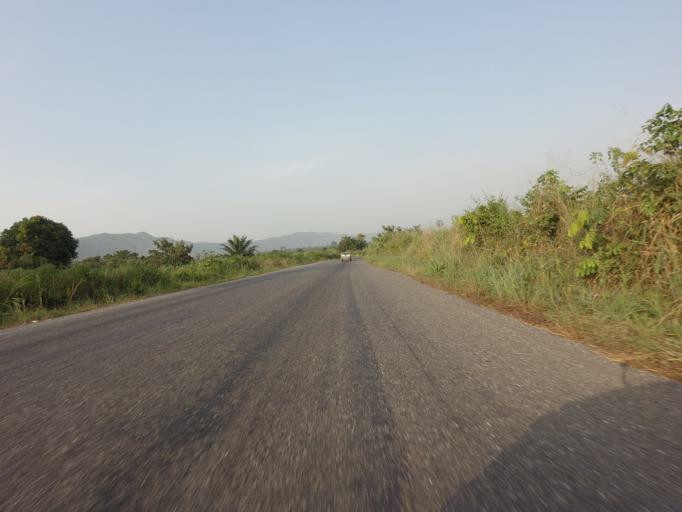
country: GH
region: Volta
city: Ho
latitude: 6.4502
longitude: 0.2118
